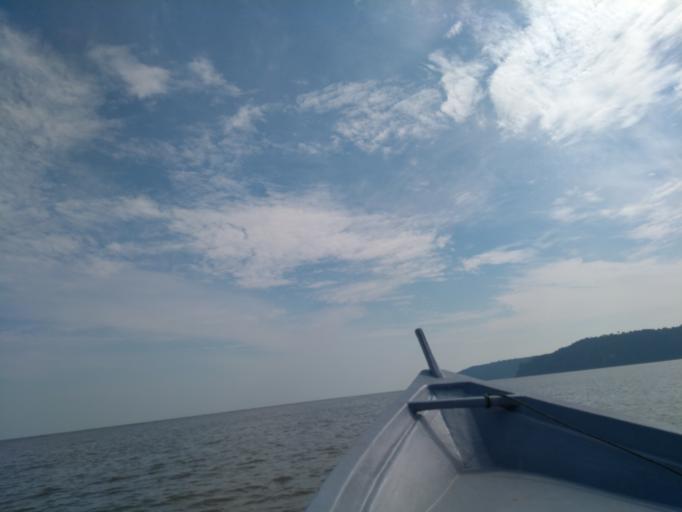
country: MY
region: Sarawak
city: Kuching
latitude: 1.7013
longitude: 110.4294
